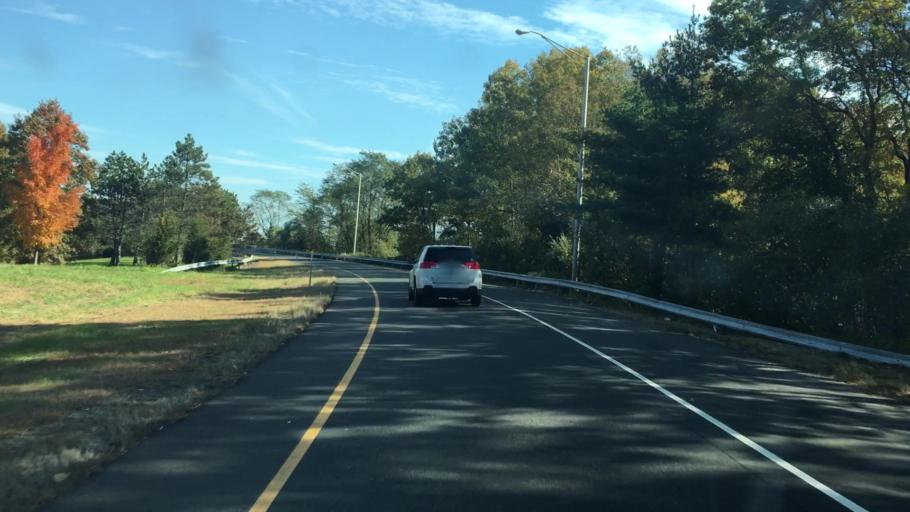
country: US
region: Connecticut
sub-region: Fairfield County
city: Trumbull
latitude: 41.2367
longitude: -73.1565
